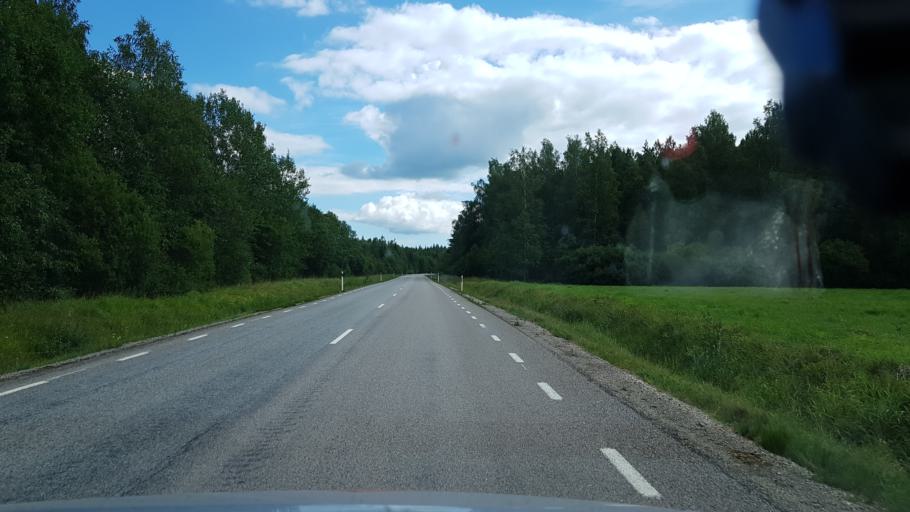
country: EE
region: Ida-Virumaa
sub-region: Kivioli linn
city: Kivioli
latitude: 59.1057
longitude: 26.9764
